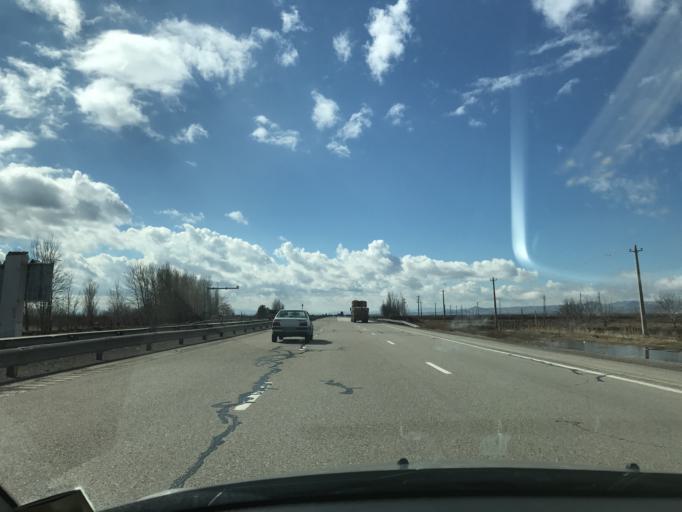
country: IR
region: Qazvin
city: Qazvin
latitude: 36.2349
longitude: 49.9033
